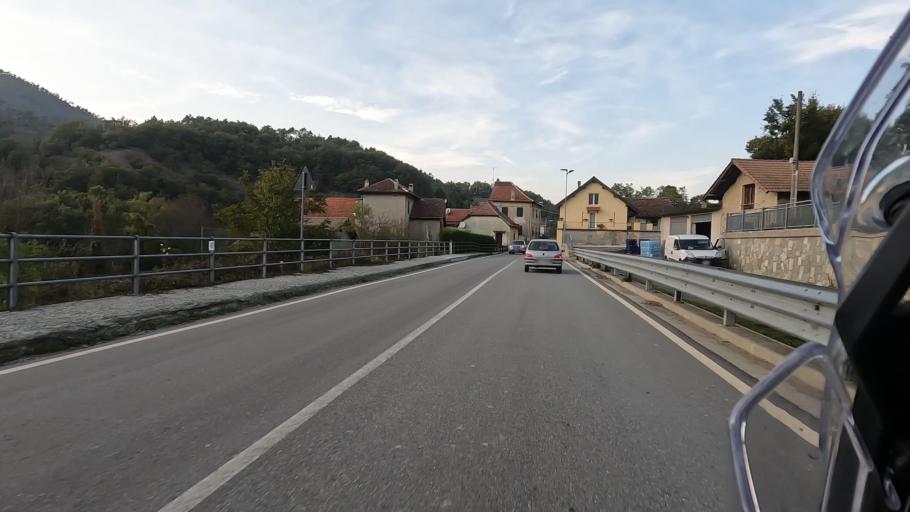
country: IT
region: Liguria
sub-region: Provincia di Savona
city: Sassello
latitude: 44.4694
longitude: 8.4843
